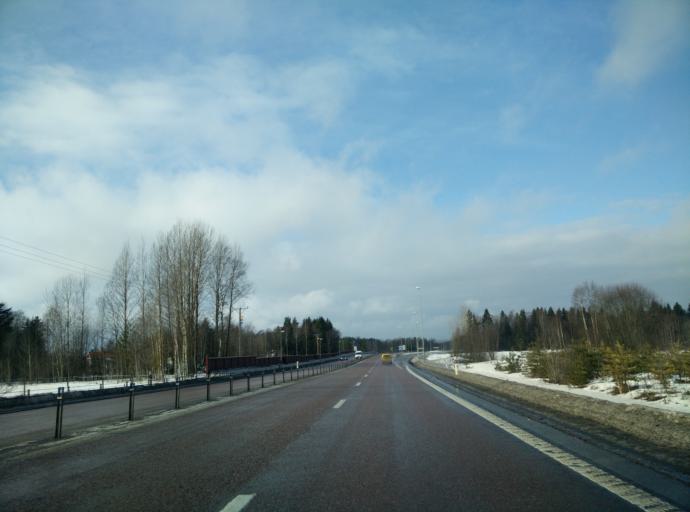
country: SE
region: Gaevleborg
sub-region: Sandvikens Kommun
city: Arsunda
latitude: 60.6097
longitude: 16.6483
